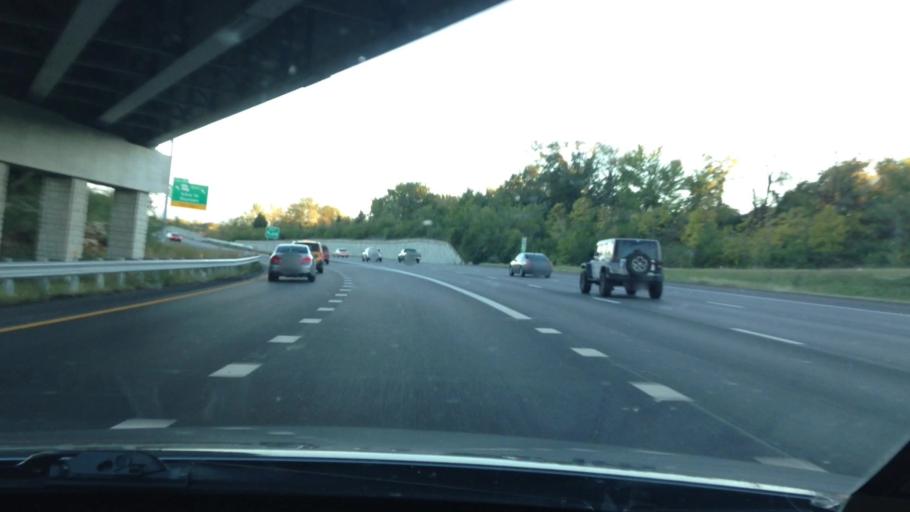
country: US
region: Missouri
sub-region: Jackson County
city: Raytown
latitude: 39.0204
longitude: -94.5011
